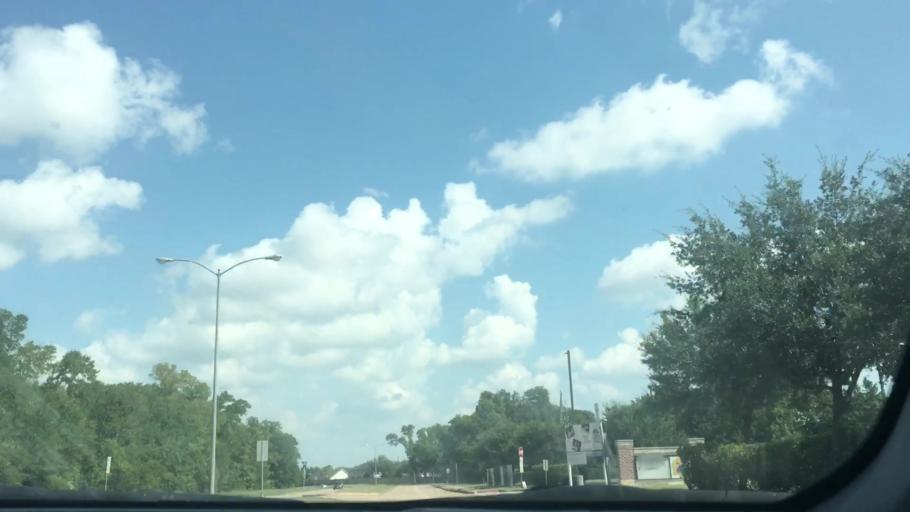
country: US
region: Texas
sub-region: Fort Bend County
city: Fifth Street
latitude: 29.5970
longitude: -95.5616
